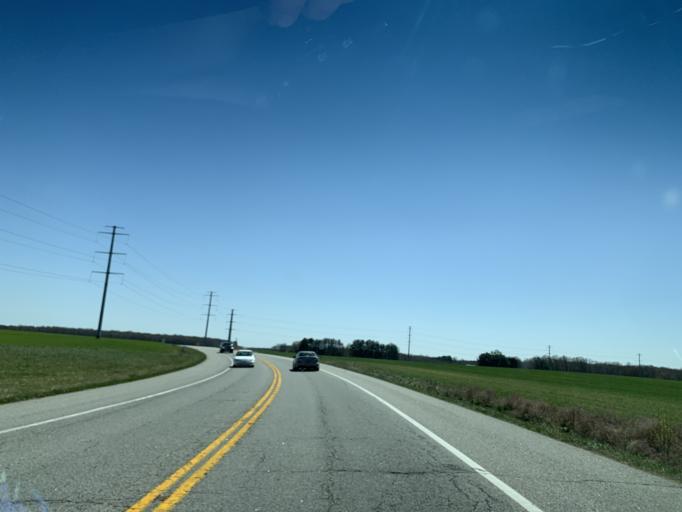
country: US
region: Maryland
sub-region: Queen Anne's County
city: Centreville
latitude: 38.9960
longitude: -76.0470
